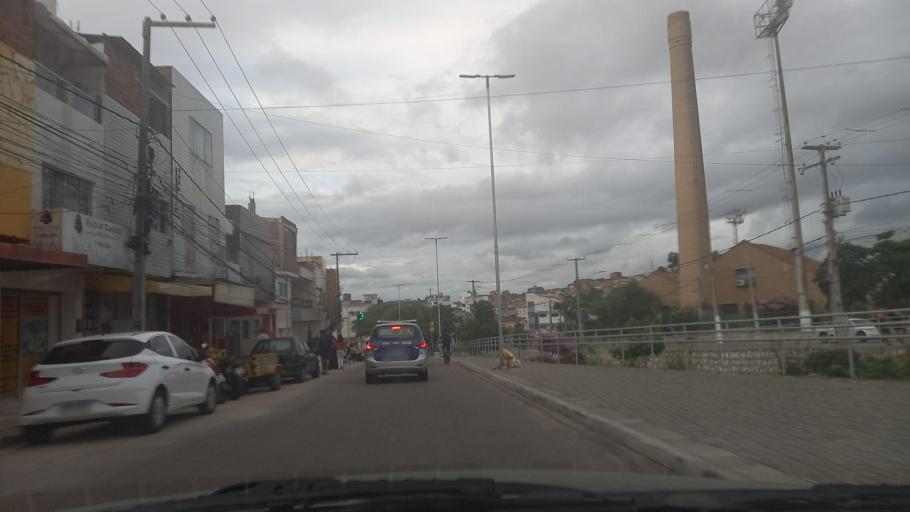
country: BR
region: Pernambuco
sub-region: Caruaru
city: Caruaru
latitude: -8.2822
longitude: -35.9667
